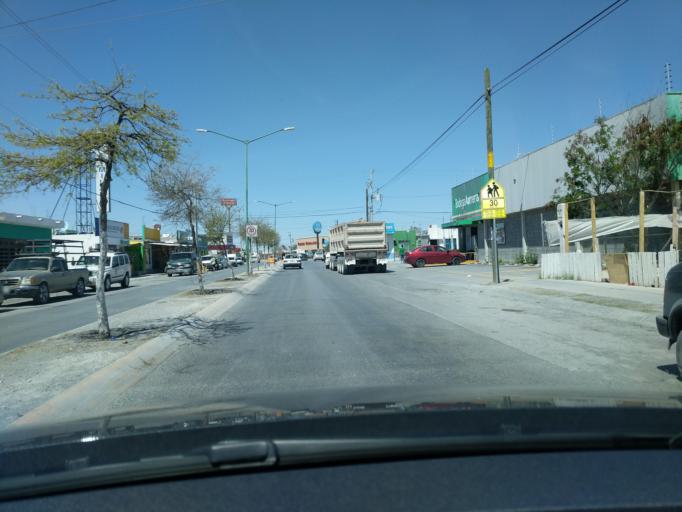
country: MX
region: Nuevo Leon
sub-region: Pesqueria
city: Colinas del Aeropuerto
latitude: 25.8255
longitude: -100.1155
